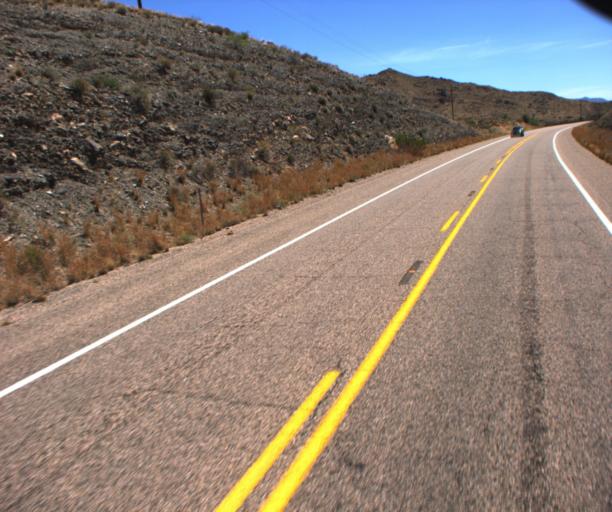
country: US
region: Arizona
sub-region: Mohave County
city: New Kingman-Butler
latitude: 35.3870
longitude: -113.7361
